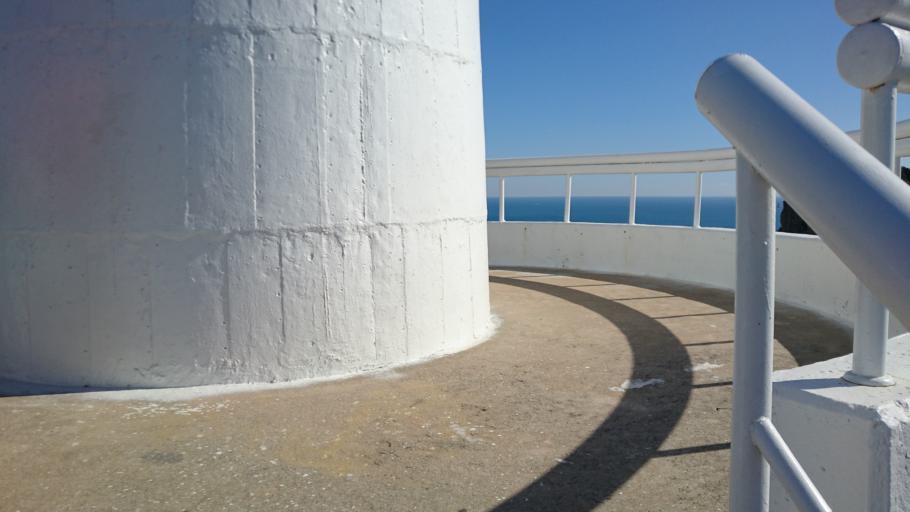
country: KR
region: Gyeongsangnam-do
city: Kyosai
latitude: 34.6196
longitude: 128.5479
